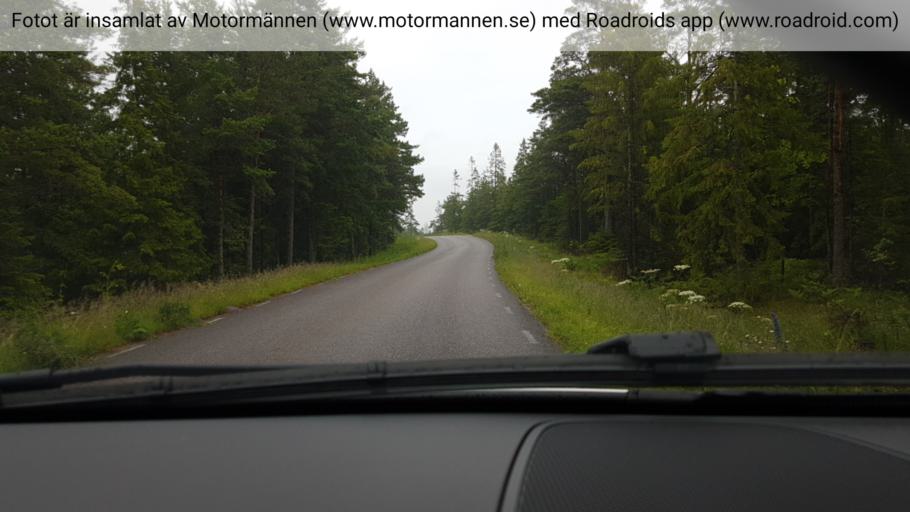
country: SE
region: Gotland
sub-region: Gotland
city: Slite
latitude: 57.8563
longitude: 18.7749
